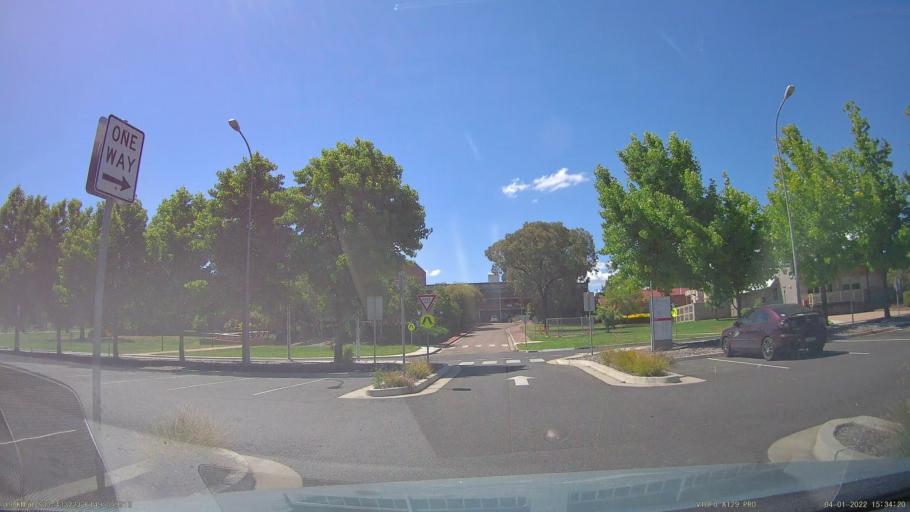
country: AU
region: New South Wales
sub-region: Bathurst Regional
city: Bathurst
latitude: -33.4332
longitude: 149.5599
